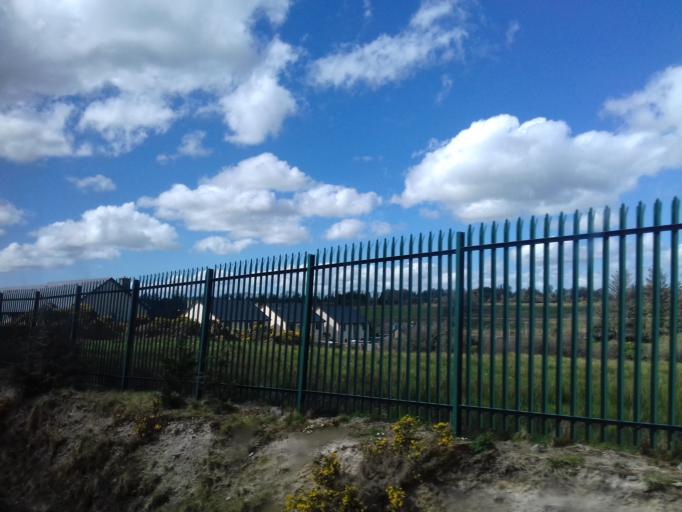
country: IE
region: Munster
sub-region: County Cork
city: Millstreet
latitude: 52.0851
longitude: -9.2142
